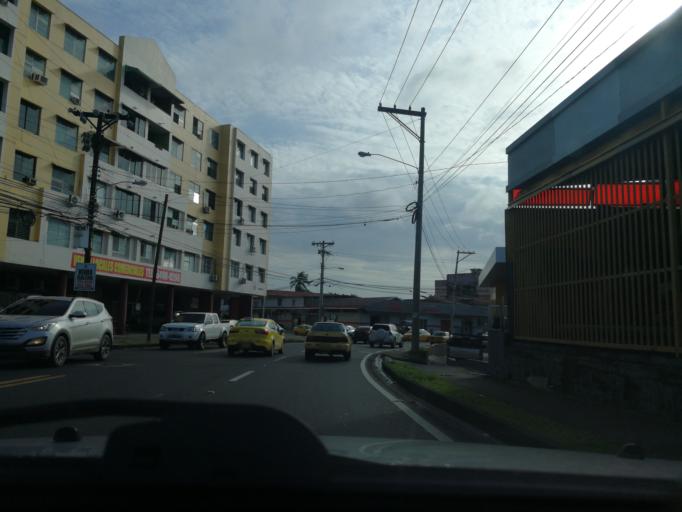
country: PA
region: Panama
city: Panama
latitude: 9.0180
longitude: -79.5027
